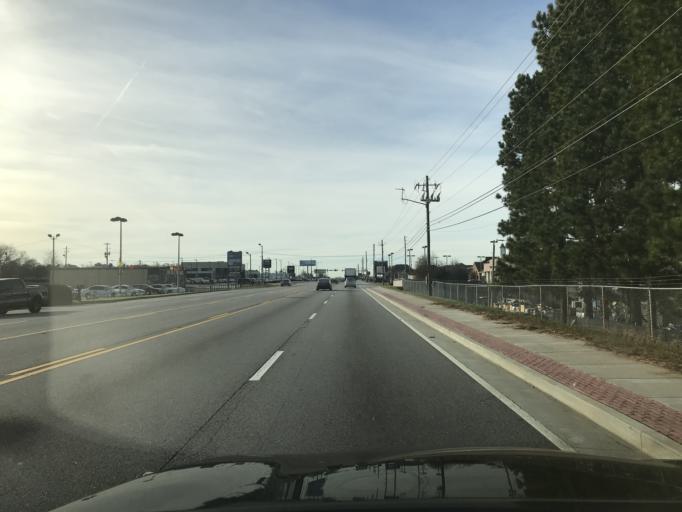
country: US
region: Georgia
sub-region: Clayton County
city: Morrow
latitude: 33.5628
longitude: -84.3449
